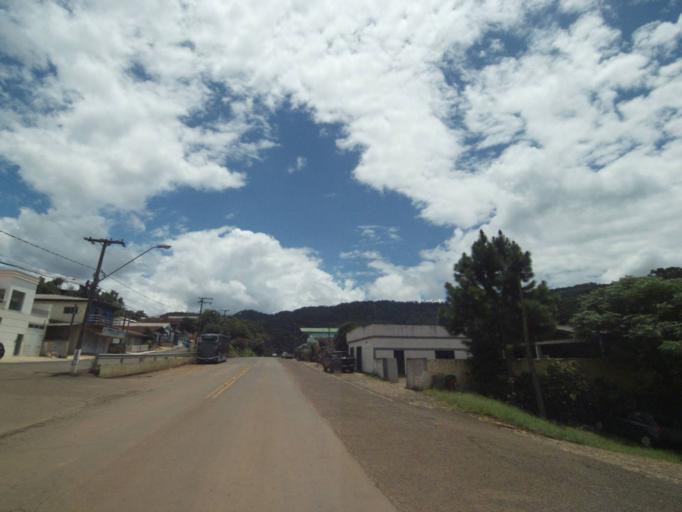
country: BR
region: Parana
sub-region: Pinhao
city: Pinhao
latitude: -26.1569
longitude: -51.5601
